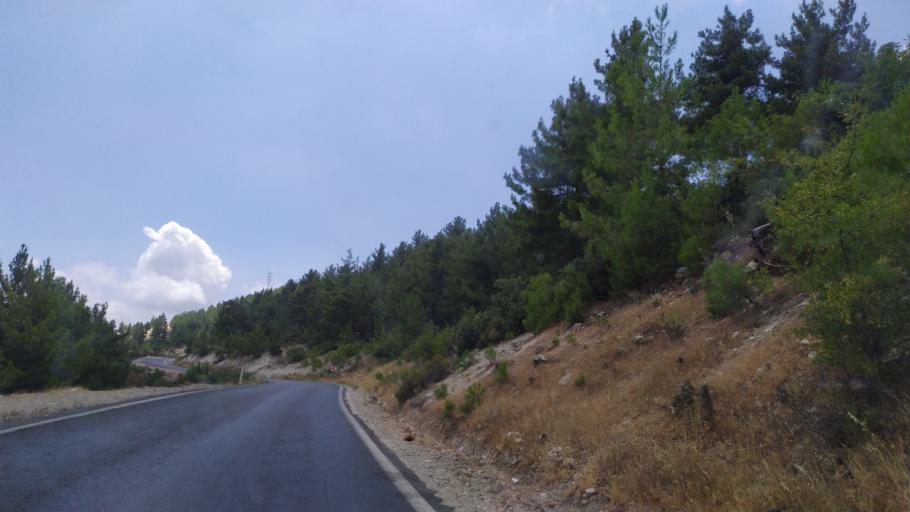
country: TR
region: Mersin
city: Gulnar
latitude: 36.2943
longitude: 33.3801
